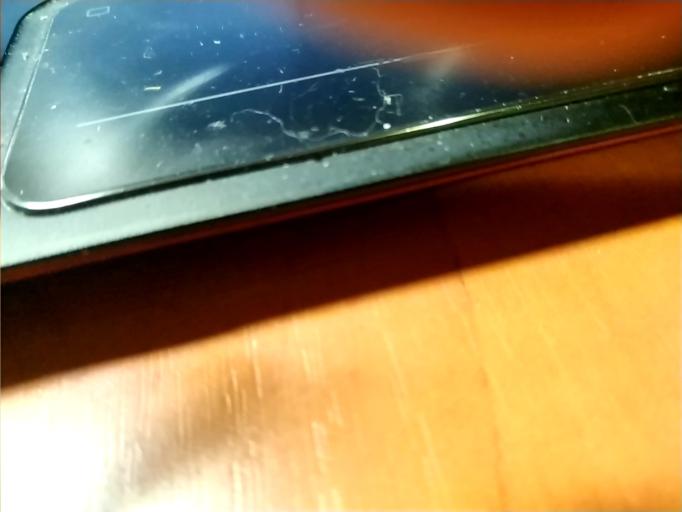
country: RU
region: Tverskaya
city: Kalashnikovo
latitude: 57.3824
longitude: 35.1538
